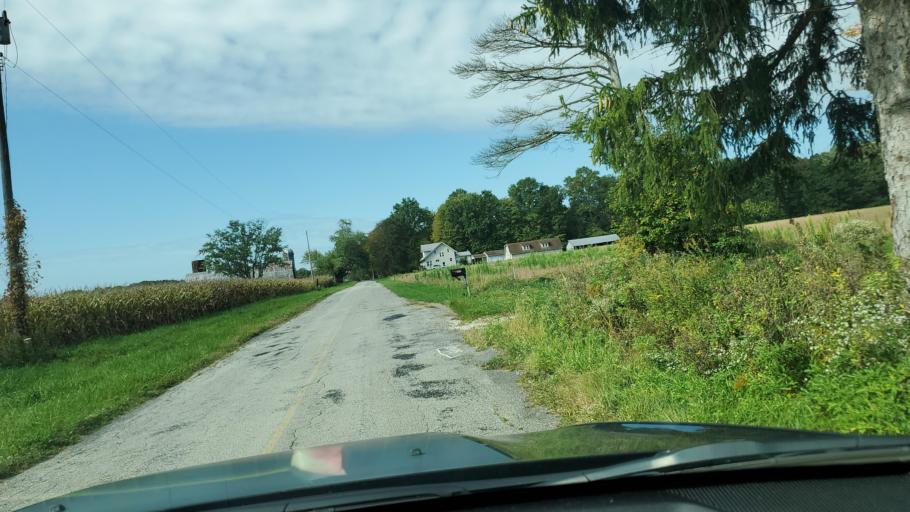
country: US
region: Ohio
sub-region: Trumbull County
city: Cortland
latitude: 41.4127
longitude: -80.6426
